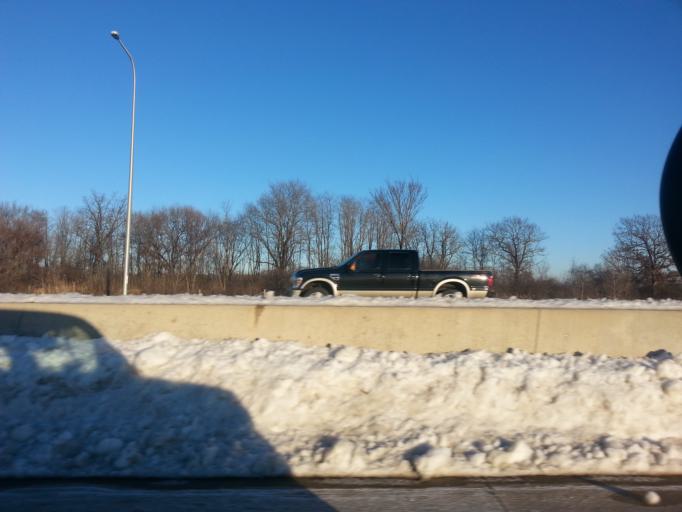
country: US
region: Wisconsin
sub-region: Kenosha County
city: Pleasant Prairie
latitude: 42.4929
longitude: -87.9493
